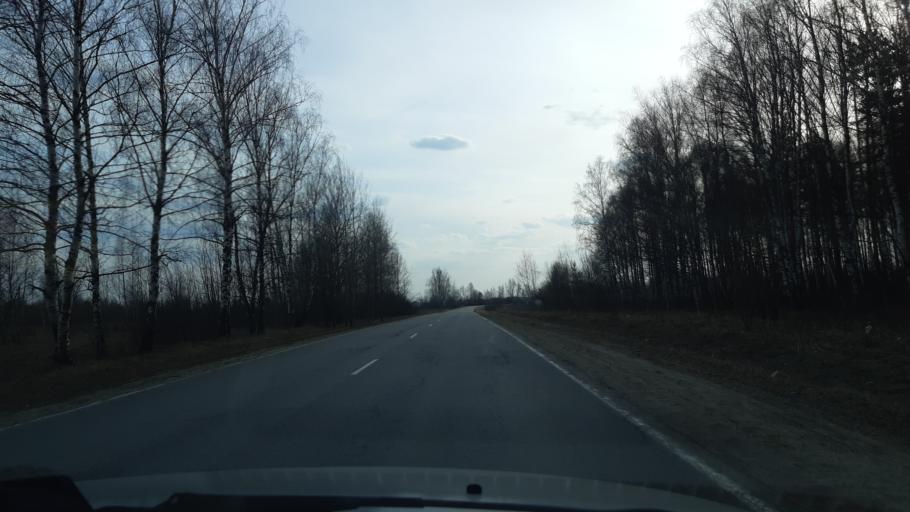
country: RU
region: Vladimir
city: Luknovo
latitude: 56.1933
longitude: 42.0294
